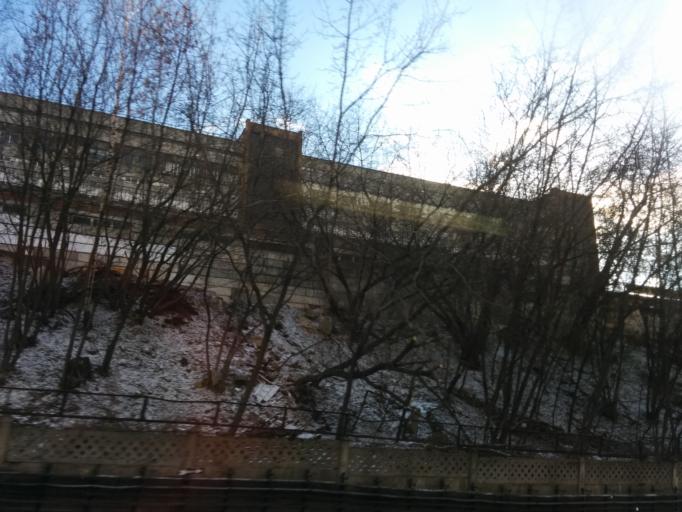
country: RU
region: Moskovskaya
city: Presnenskiy
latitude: 55.7435
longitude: 37.5273
